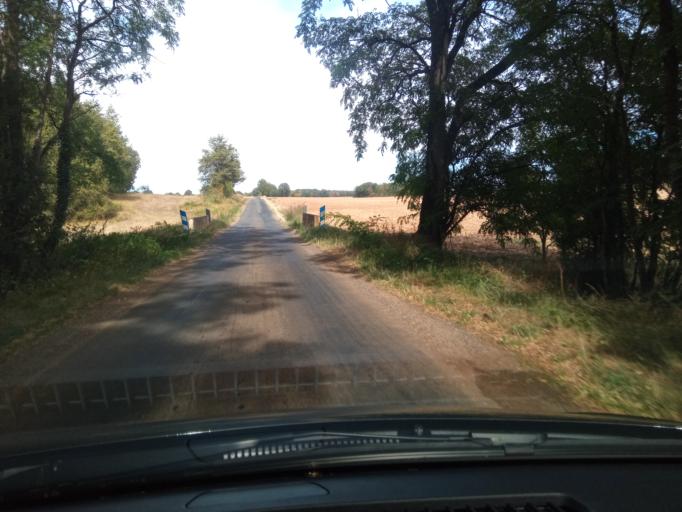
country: FR
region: Poitou-Charentes
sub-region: Departement de la Vienne
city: Chauvigny
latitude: 46.5308
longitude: 0.7367
